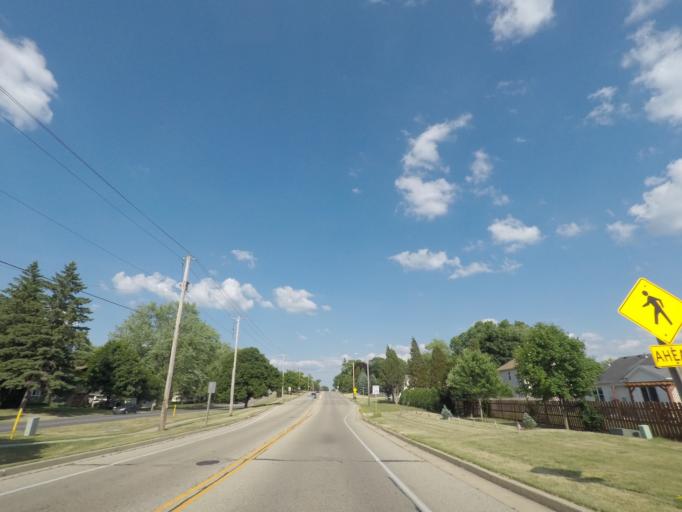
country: US
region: Wisconsin
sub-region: Walworth County
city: East Troy
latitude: 42.7923
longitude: -88.4016
